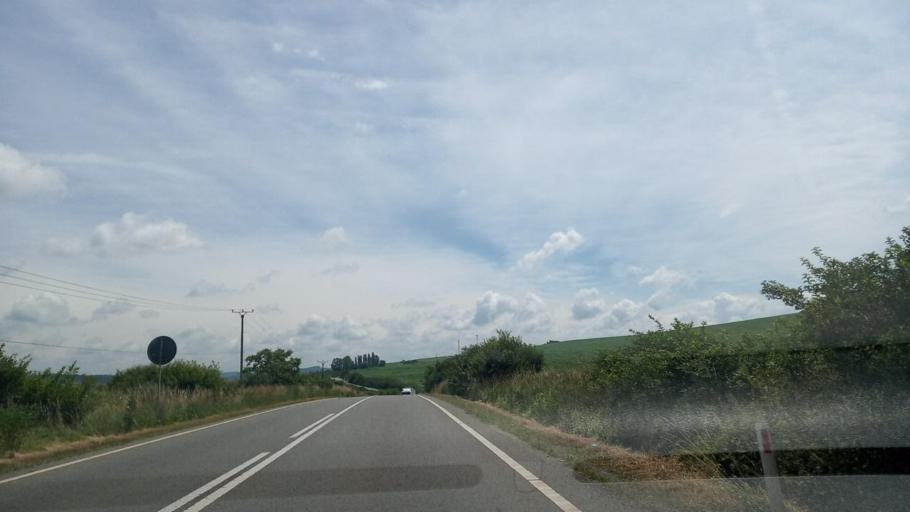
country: RO
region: Alba
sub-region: Comuna Cut
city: Cut
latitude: 45.9198
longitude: 23.6456
